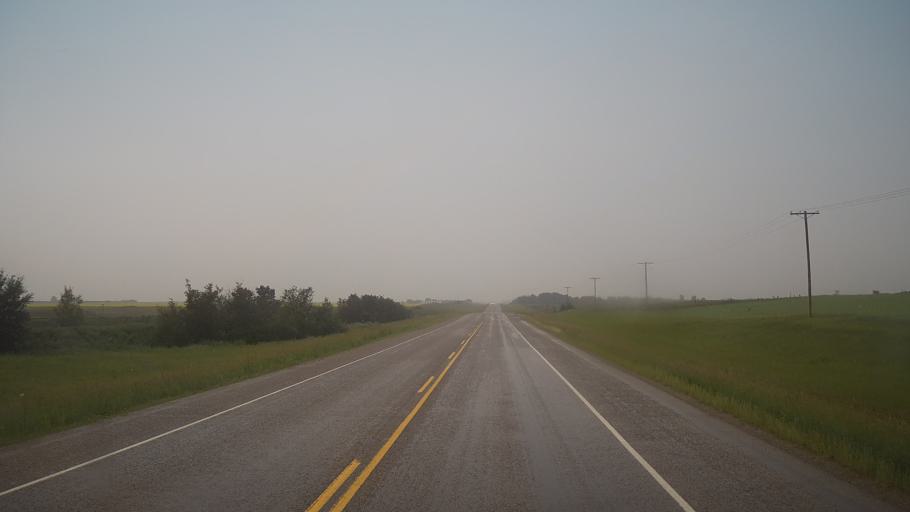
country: CA
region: Saskatchewan
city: Biggar
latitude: 52.1307
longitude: -108.1482
